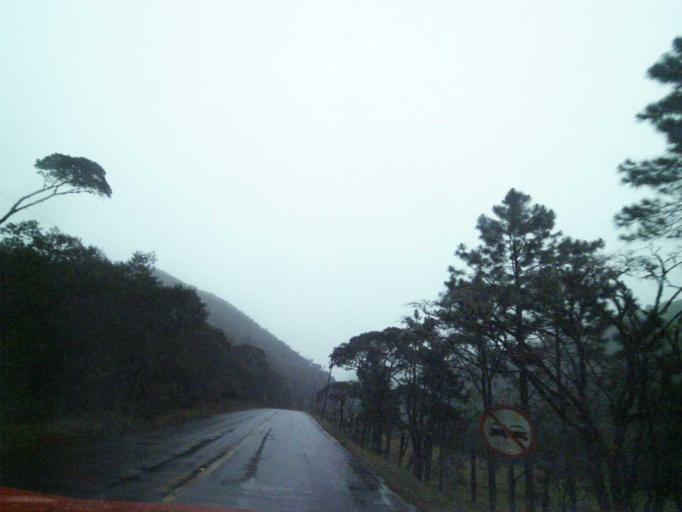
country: BR
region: Santa Catarina
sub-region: Anitapolis
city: Anitapolis
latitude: -27.7579
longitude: -49.0363
